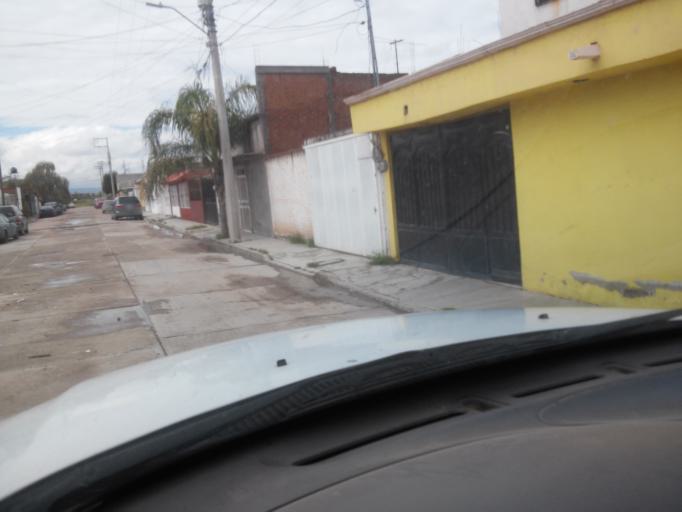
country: MX
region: Durango
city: Victoria de Durango
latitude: 24.0237
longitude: -104.6153
